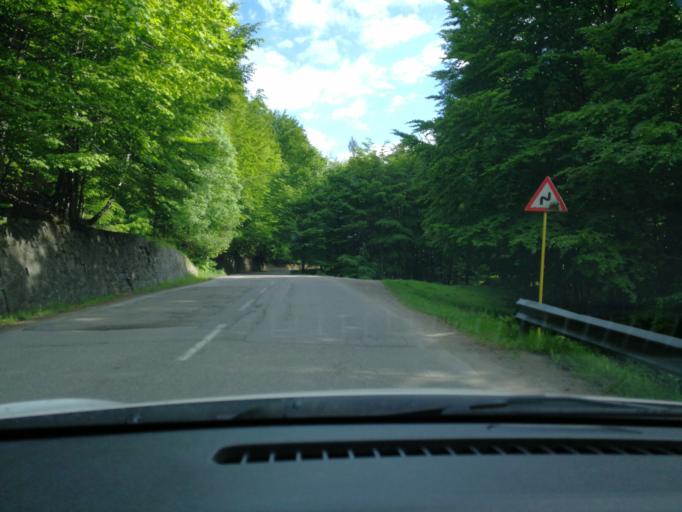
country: RO
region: Prahova
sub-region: Comuna Valea Doftanei
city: Tesila
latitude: 45.2624
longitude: 25.7346
